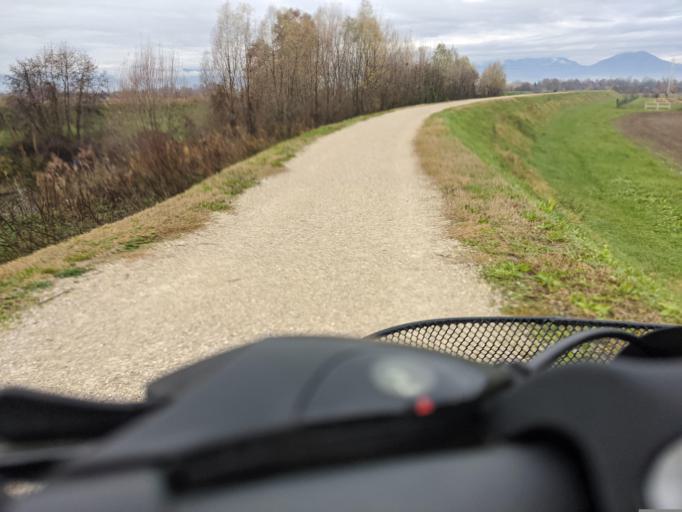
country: IT
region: Veneto
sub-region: Provincia di Vicenza
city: Dueville
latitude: 45.6116
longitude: 11.5418
